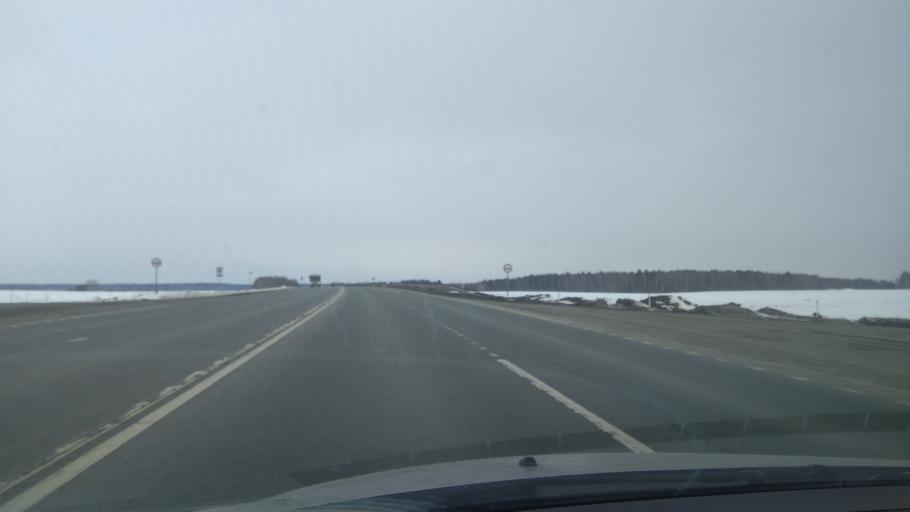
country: RU
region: Sverdlovsk
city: Ufimskiy
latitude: 56.7737
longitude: 58.0518
